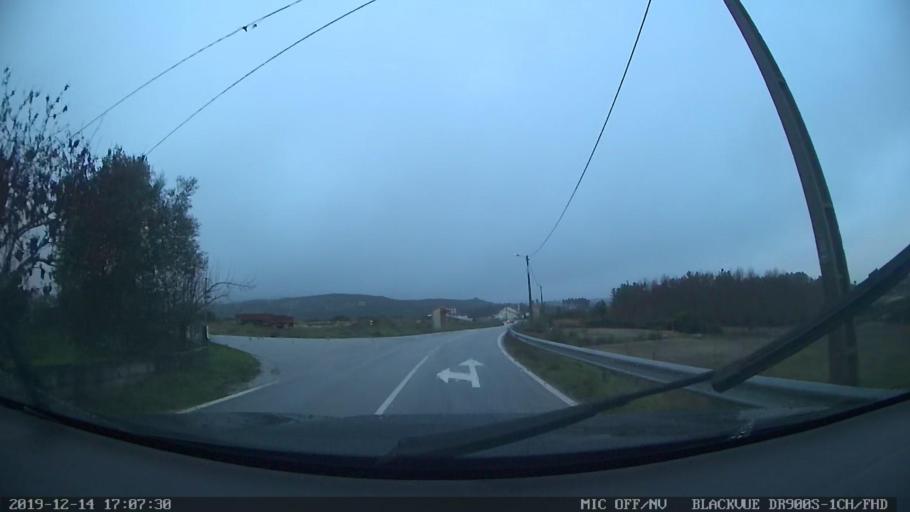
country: PT
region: Vila Real
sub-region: Vila Pouca de Aguiar
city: Vila Pouca de Aguiar
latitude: 41.4622
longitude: -7.5986
